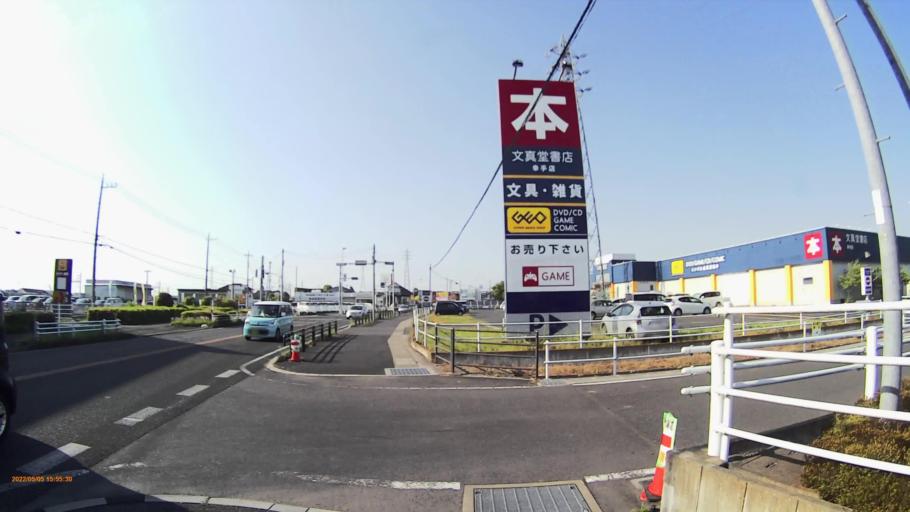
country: JP
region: Saitama
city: Satte
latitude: 36.0571
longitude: 139.7148
